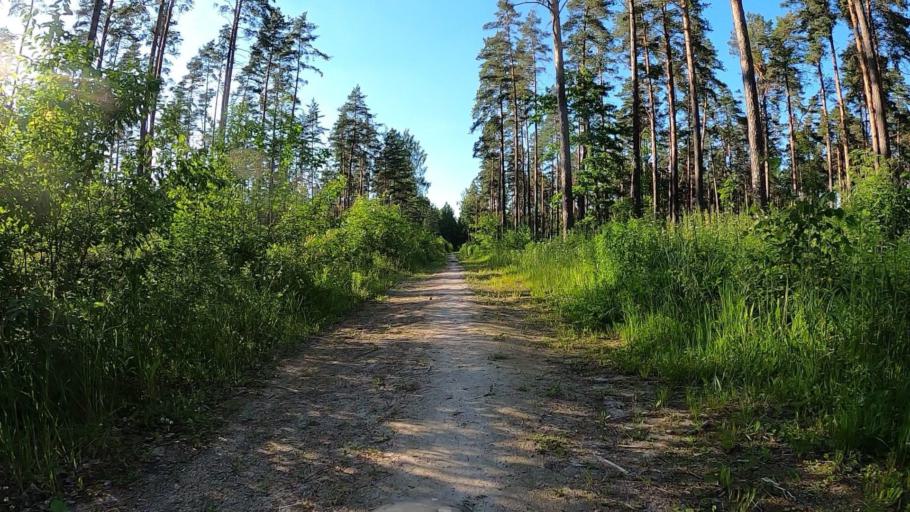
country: LV
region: Stopini
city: Ulbroka
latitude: 56.9253
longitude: 24.2351
